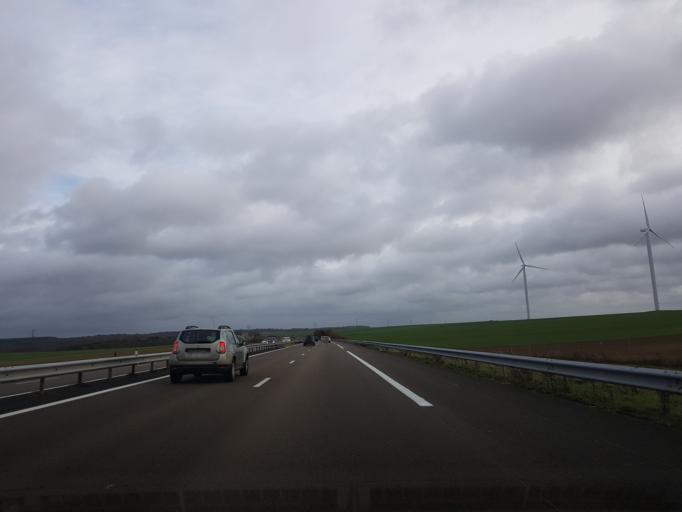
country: FR
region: Champagne-Ardenne
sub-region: Departement de l'Aube
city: Vendeuvre-sur-Barse
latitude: 48.1662
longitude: 4.5325
